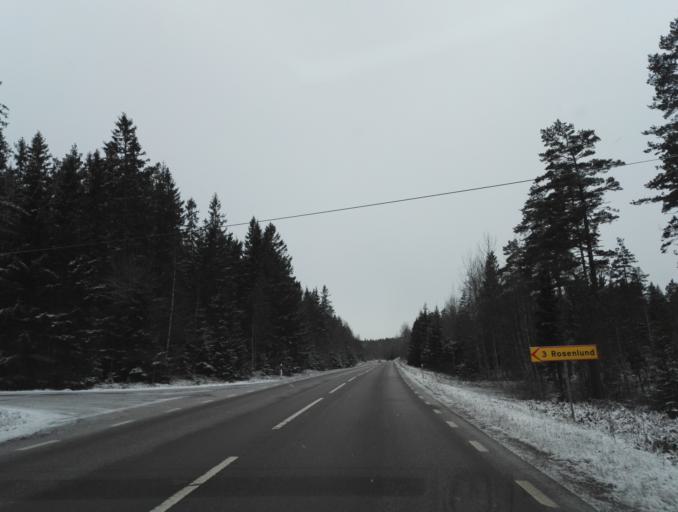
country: SE
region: Kalmar
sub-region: Hultsfreds Kommun
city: Virserum
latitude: 57.1832
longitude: 15.5017
